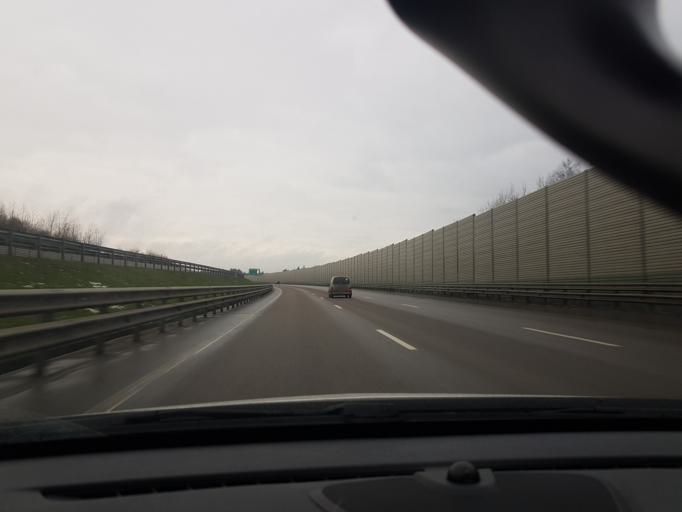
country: RU
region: Moskovskaya
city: Novopetrovskoye
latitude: 55.9733
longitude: 36.4849
